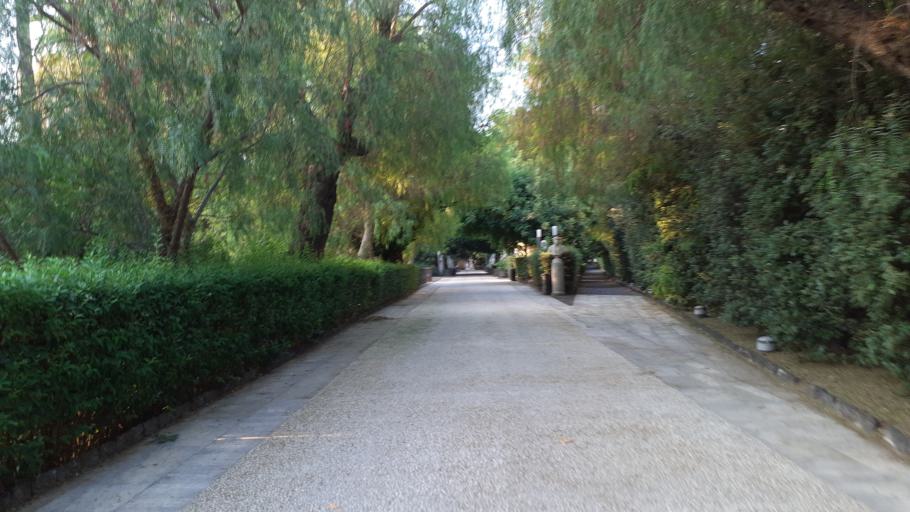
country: IT
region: Sicily
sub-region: Catania
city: Catania
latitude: 37.5111
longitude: 15.0825
